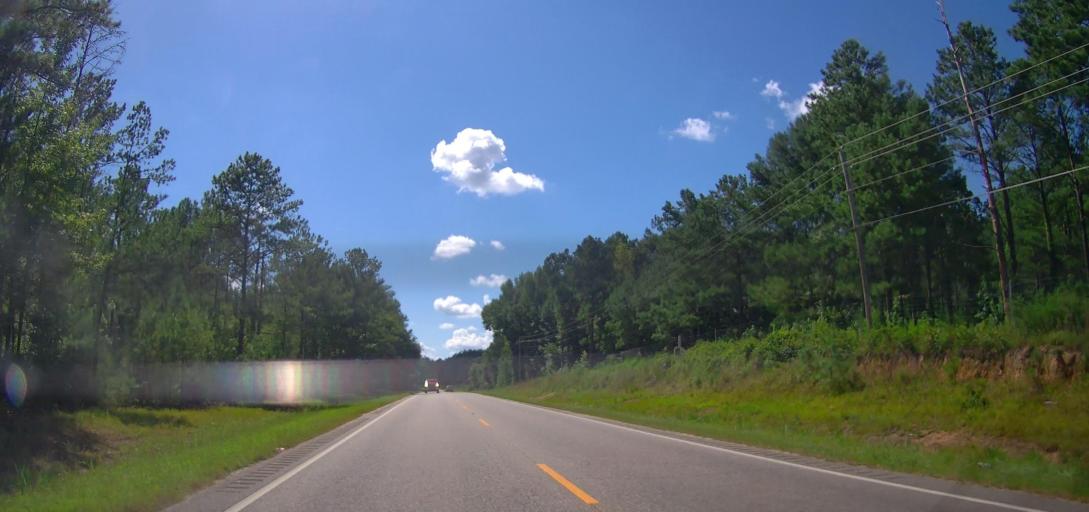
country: US
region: Alabama
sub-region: Macon County
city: Tuskegee
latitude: 32.3831
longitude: -85.8066
